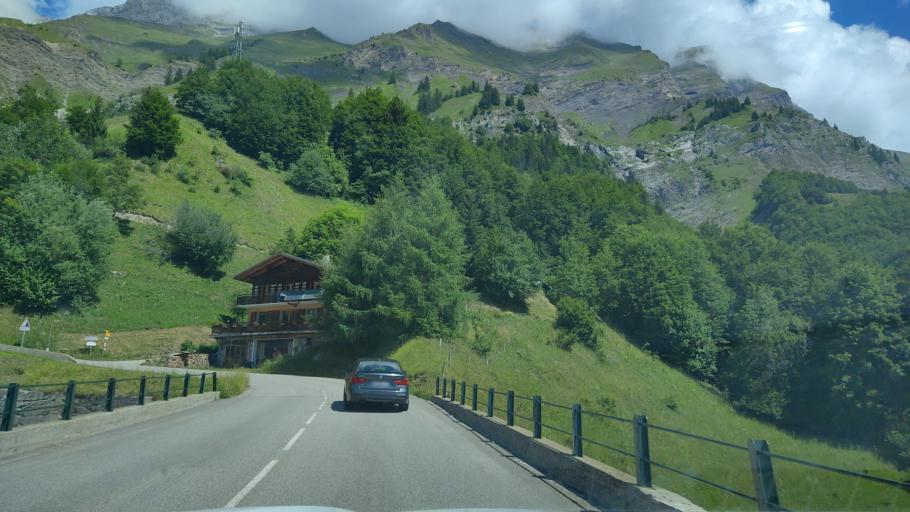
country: FR
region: Rhone-Alpes
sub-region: Departement de la Haute-Savoie
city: La Clusaz
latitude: 45.8713
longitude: 6.4868
